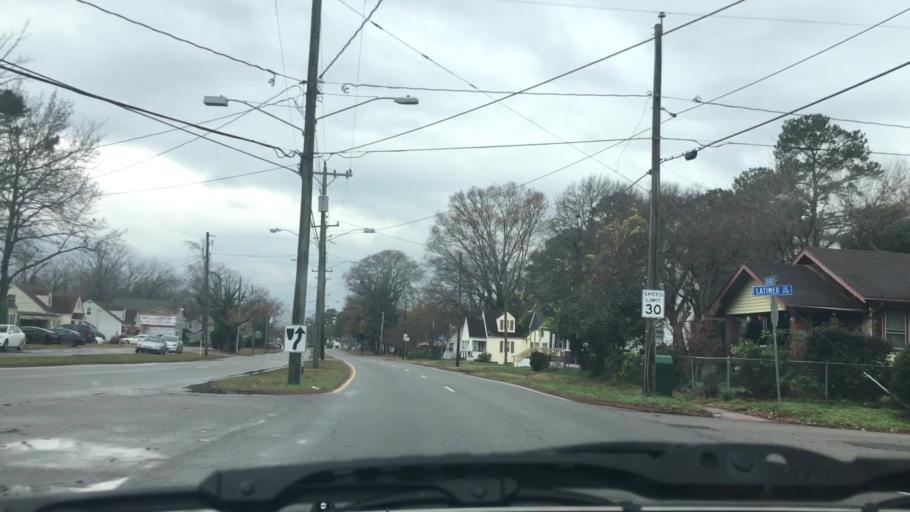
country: US
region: Virginia
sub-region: City of Norfolk
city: Norfolk
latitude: 36.8884
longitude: -76.2409
